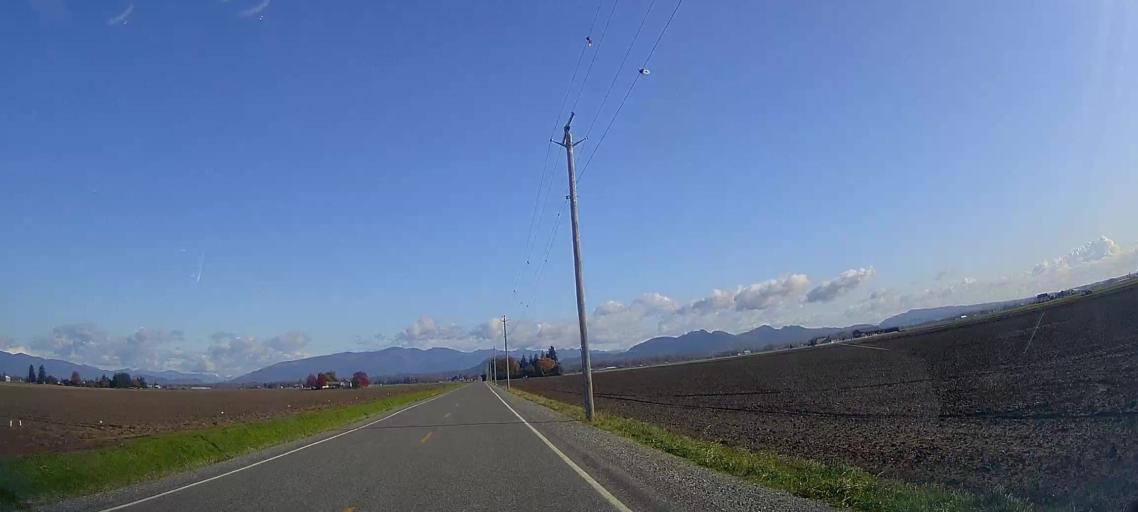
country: US
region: Washington
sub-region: Skagit County
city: Mount Vernon
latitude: 48.3990
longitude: -122.4302
